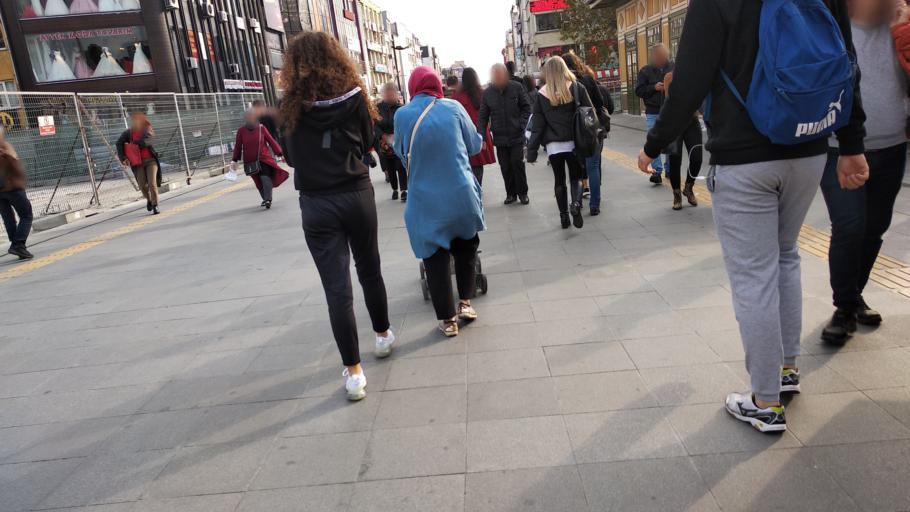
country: TR
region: Istanbul
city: Bahcelievler
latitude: 40.9806
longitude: 28.8739
